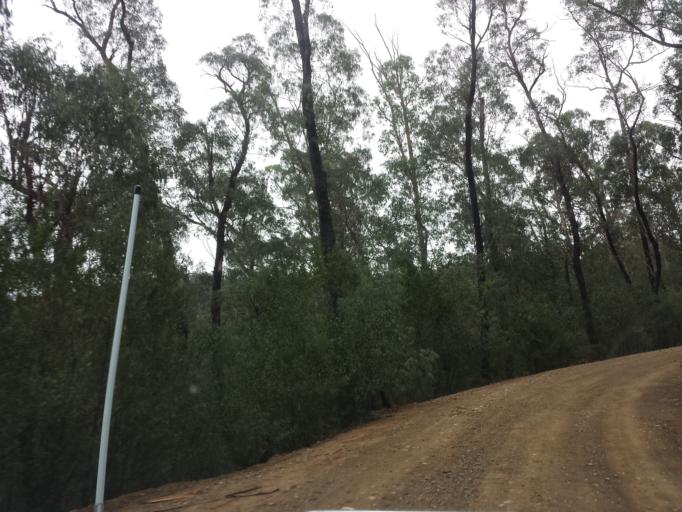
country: AU
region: Victoria
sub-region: Latrobe
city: Traralgon
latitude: -37.9994
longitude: 146.4706
